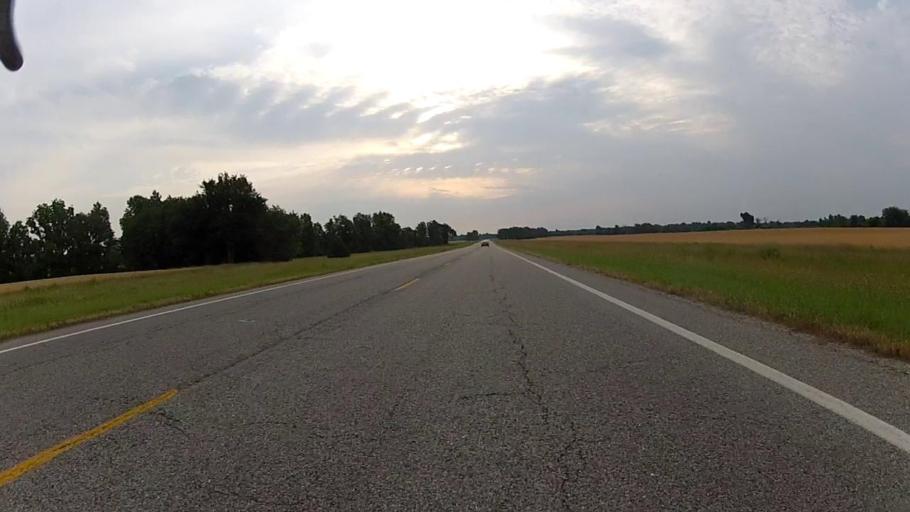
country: US
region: Kansas
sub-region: Labette County
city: Oswego
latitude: 37.1780
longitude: -94.9917
